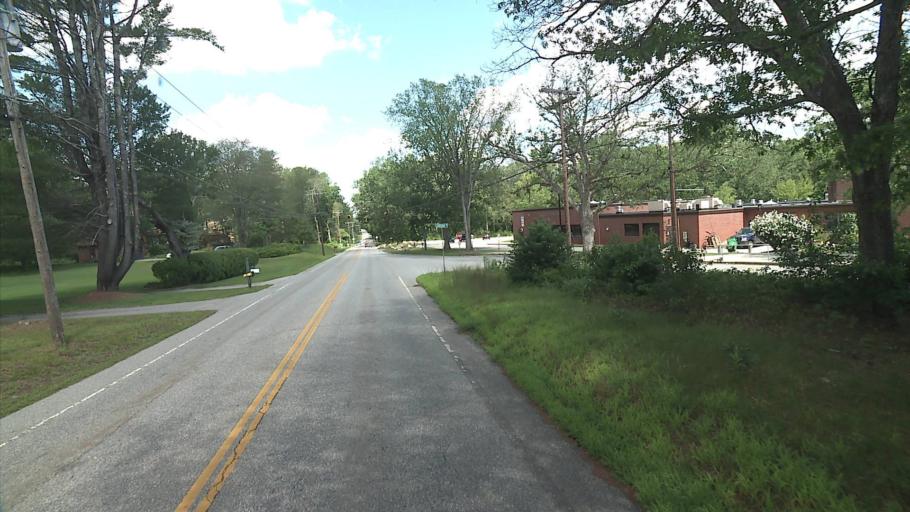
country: US
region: Connecticut
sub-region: Windham County
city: Windham
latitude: 41.7409
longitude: -72.1580
